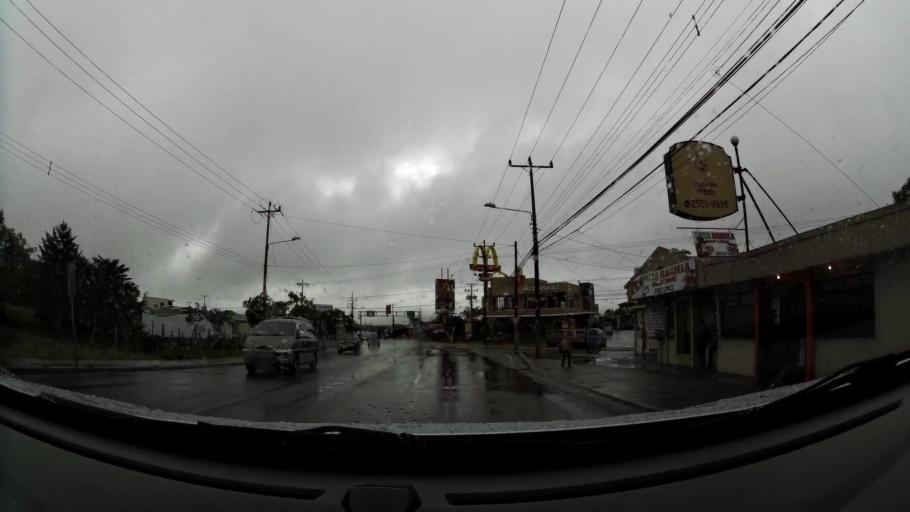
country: CR
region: Cartago
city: Cartago
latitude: 9.8565
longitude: -83.9047
